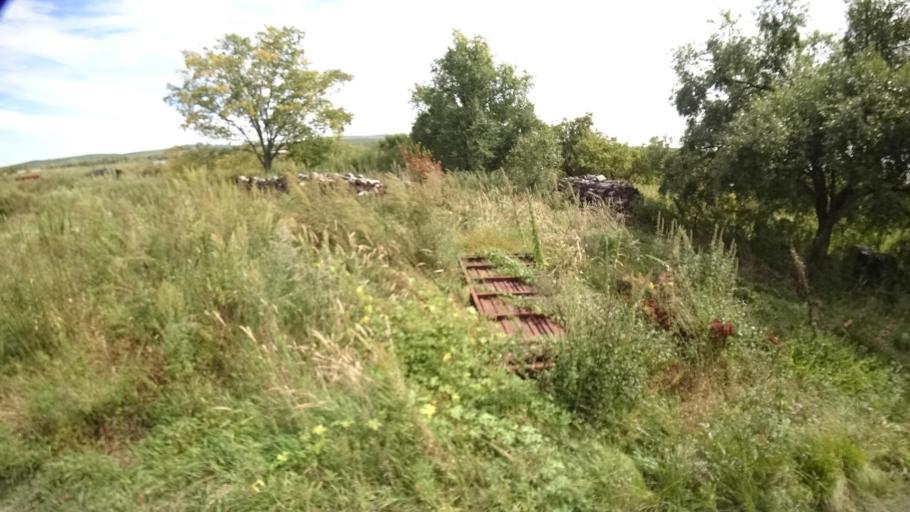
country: RU
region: Primorskiy
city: Yakovlevka
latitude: 44.6415
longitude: 133.6025
